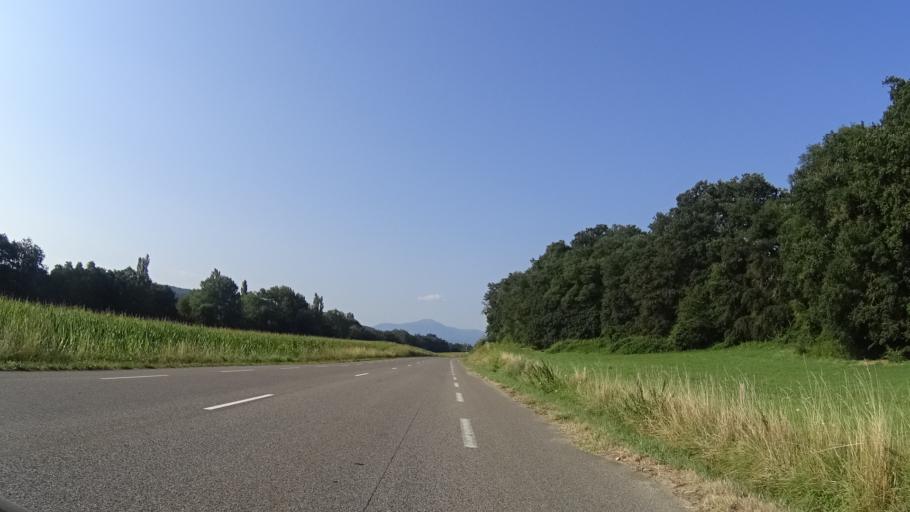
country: FR
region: Midi-Pyrenees
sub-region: Departement de l'Ariege
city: Mirepoix
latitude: 43.0221
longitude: 1.8931
